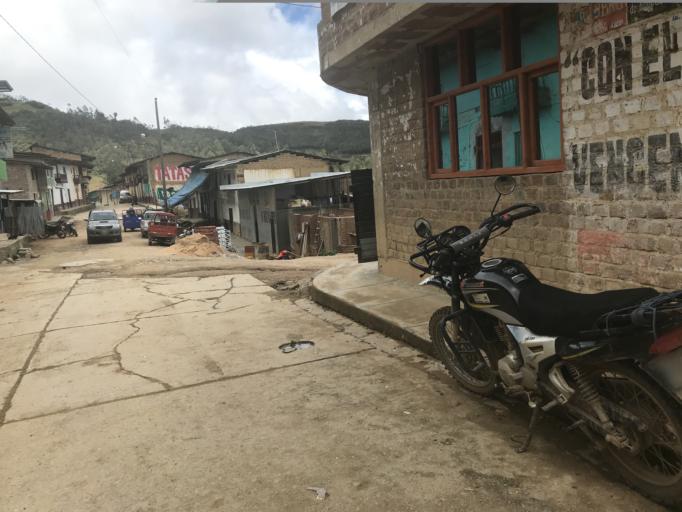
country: PE
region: Cajamarca
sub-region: Provincia de Chota
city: Querocoto
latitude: -6.3608
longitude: -79.0335
